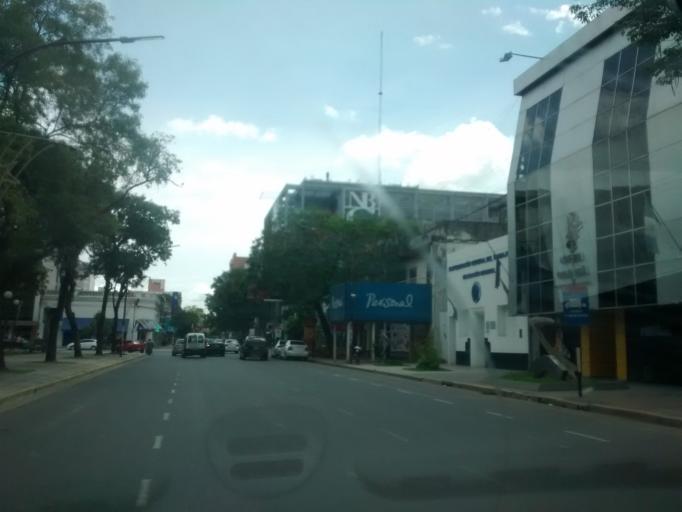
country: AR
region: Chaco
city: Resistencia
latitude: -27.4517
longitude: -58.9853
